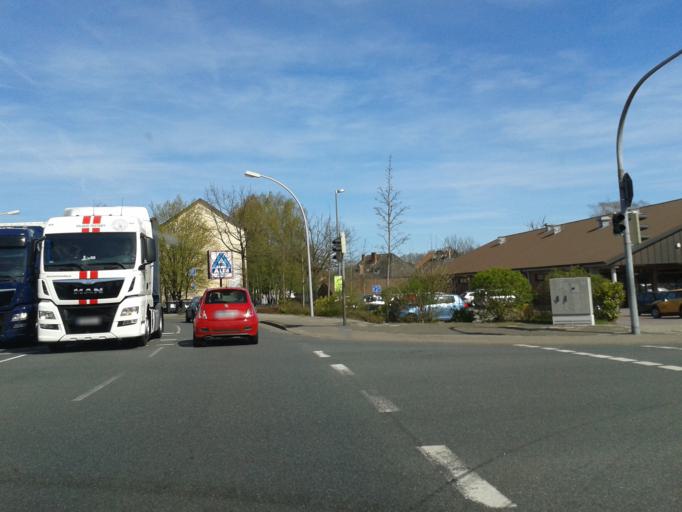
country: DE
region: Lower Saxony
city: Munster
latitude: 52.9852
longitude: 10.0871
